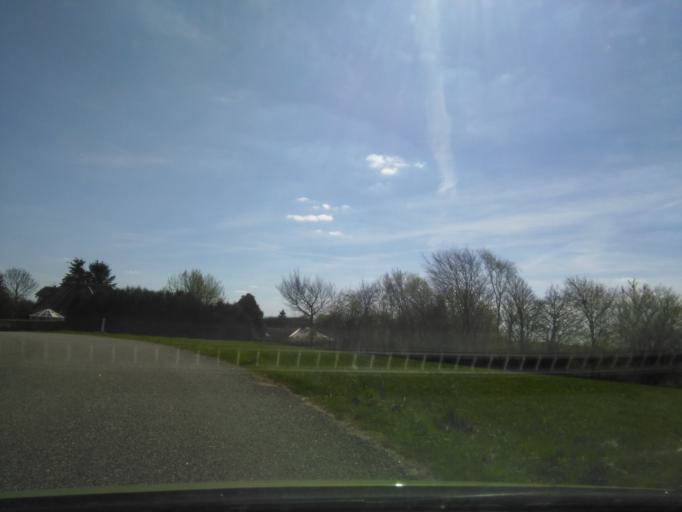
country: DK
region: Central Jutland
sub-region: Silkeborg Kommune
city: Kjellerup
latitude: 56.3532
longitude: 9.3384
